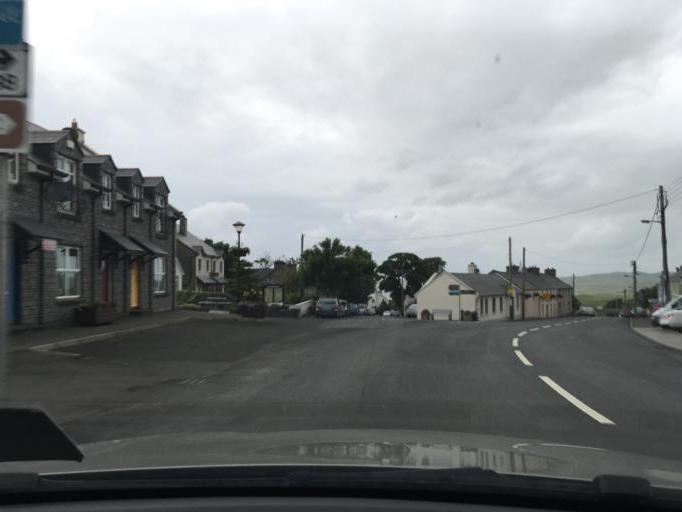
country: IE
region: Ulster
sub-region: County Donegal
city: Carndonagh
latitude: 55.2793
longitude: -7.3941
